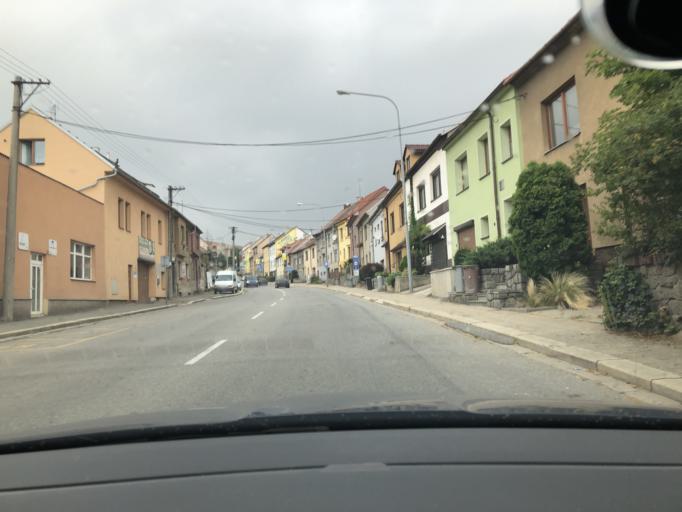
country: CZ
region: Vysocina
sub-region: Okres Trebic
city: Trebic
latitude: 49.2185
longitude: 15.8715
